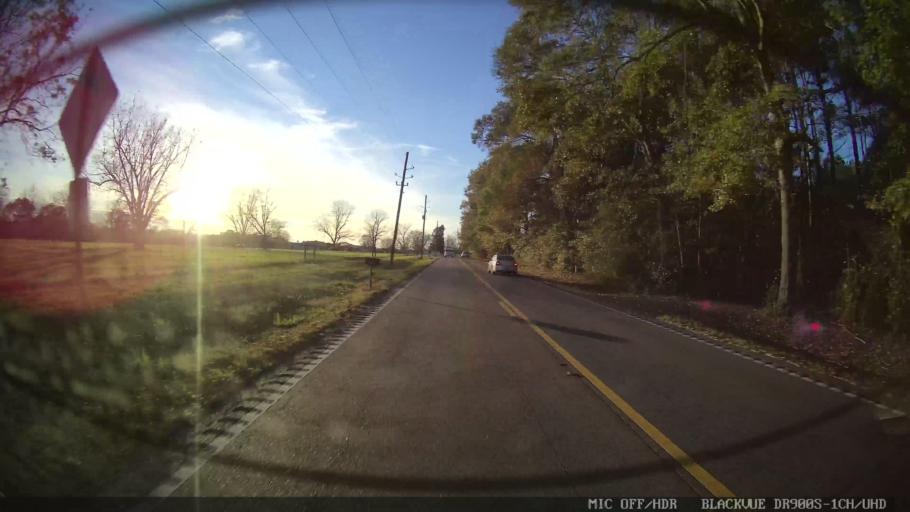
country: US
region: Mississippi
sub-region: Lamar County
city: Lumberton
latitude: 30.9958
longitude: -89.3883
